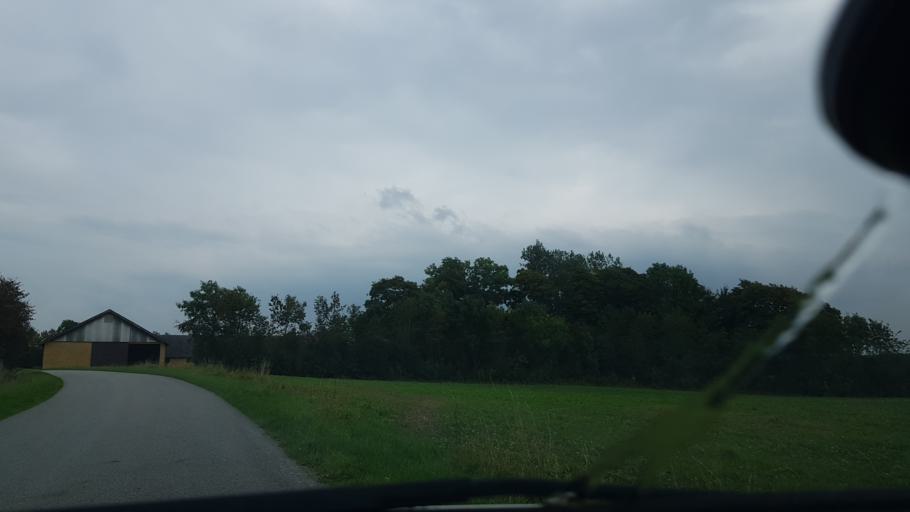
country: DK
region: South Denmark
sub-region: Vejle Kommune
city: Egtved
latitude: 55.5716
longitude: 9.2617
